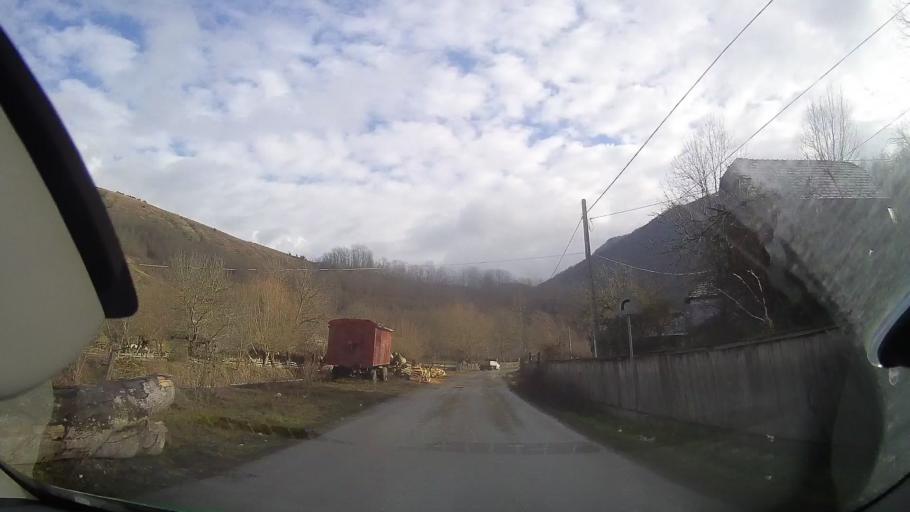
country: RO
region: Alba
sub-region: Comuna Ocolis
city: Ocolis
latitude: 46.4714
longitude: 23.4730
